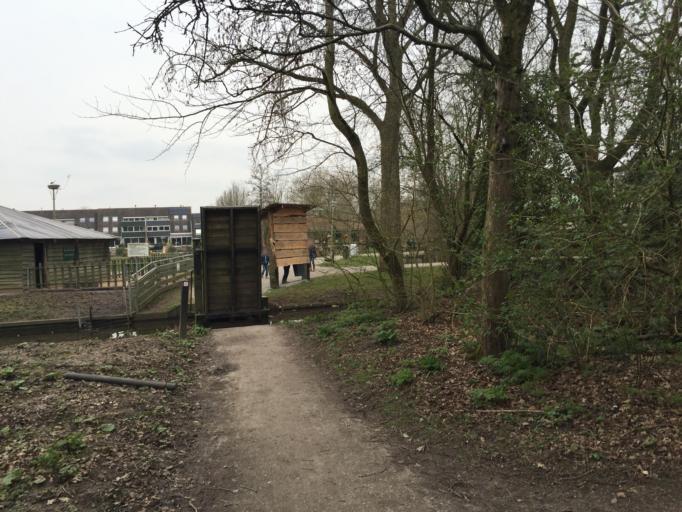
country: NL
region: South Holland
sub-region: Gemeente Leiden
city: Leiden
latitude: 52.1781
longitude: 4.5079
